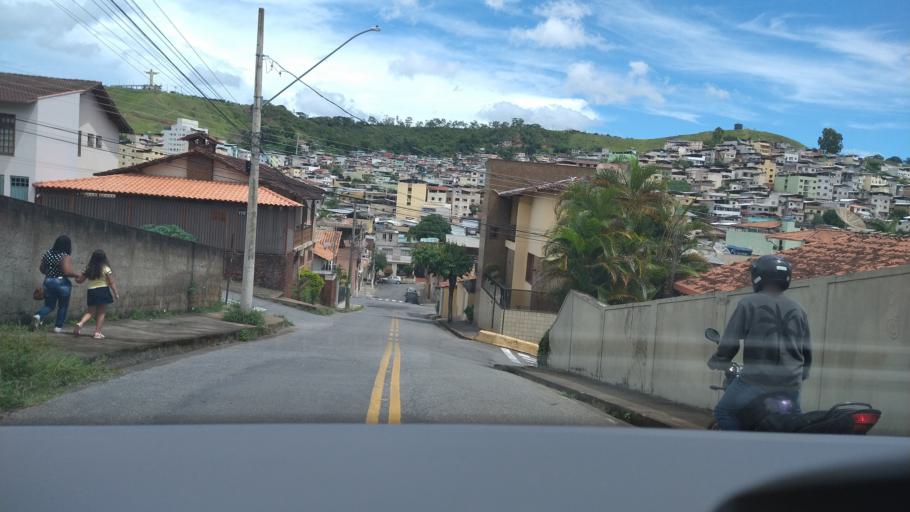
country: BR
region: Minas Gerais
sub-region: Vicosa
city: Vicosa
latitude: -20.7638
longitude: -42.8853
